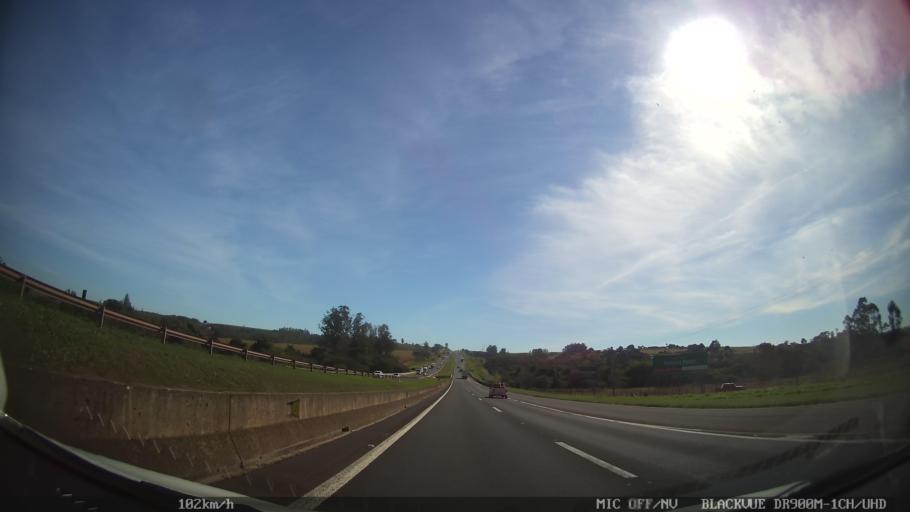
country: BR
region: Sao Paulo
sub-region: Leme
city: Leme
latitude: -22.1008
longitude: -47.4151
